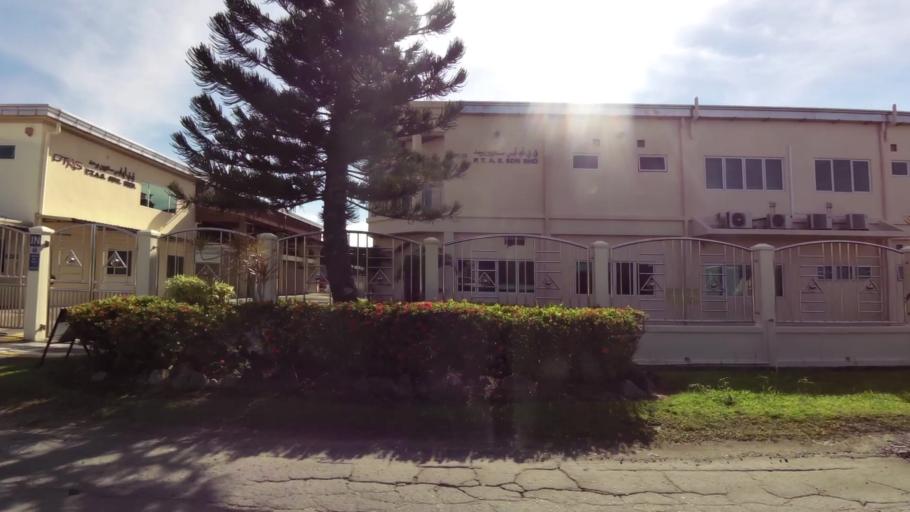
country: BN
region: Belait
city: Kuala Belait
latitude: 4.5723
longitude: 114.2093
